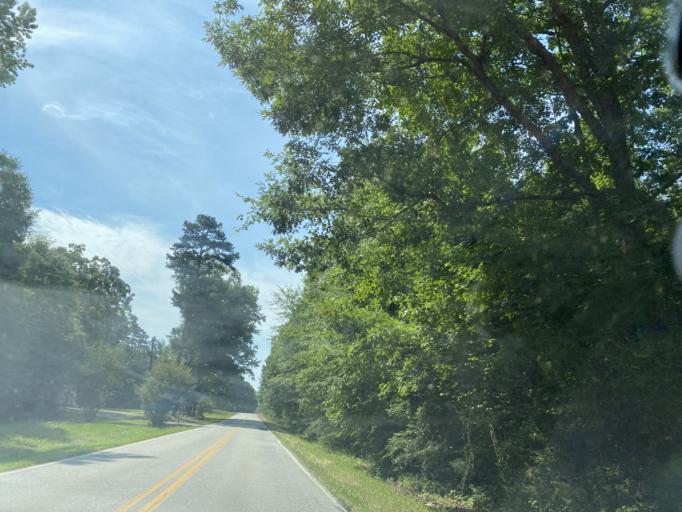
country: US
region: Georgia
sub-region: Coweta County
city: Grantville
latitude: 33.1890
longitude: -84.7110
